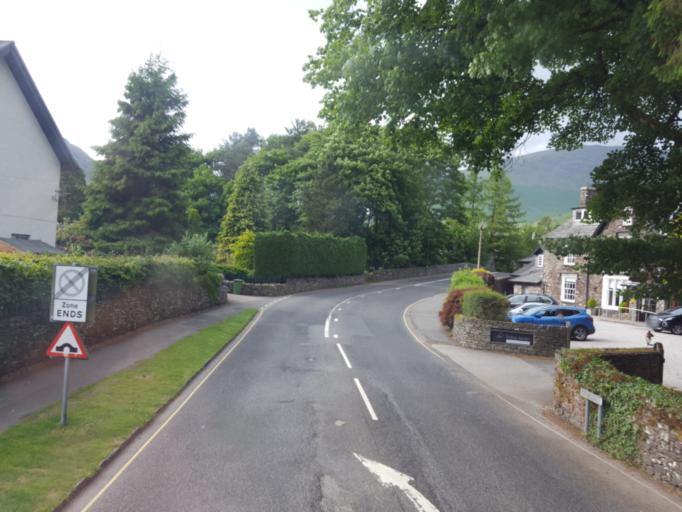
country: GB
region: England
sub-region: Cumbria
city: Ambleside
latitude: 54.4625
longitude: -3.0225
